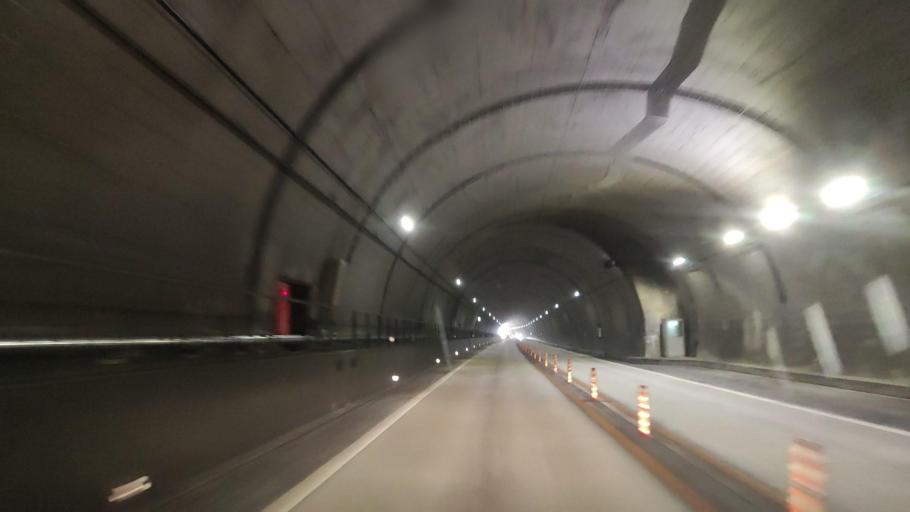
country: JP
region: Ehime
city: Hojo
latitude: 34.0839
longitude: 132.9775
